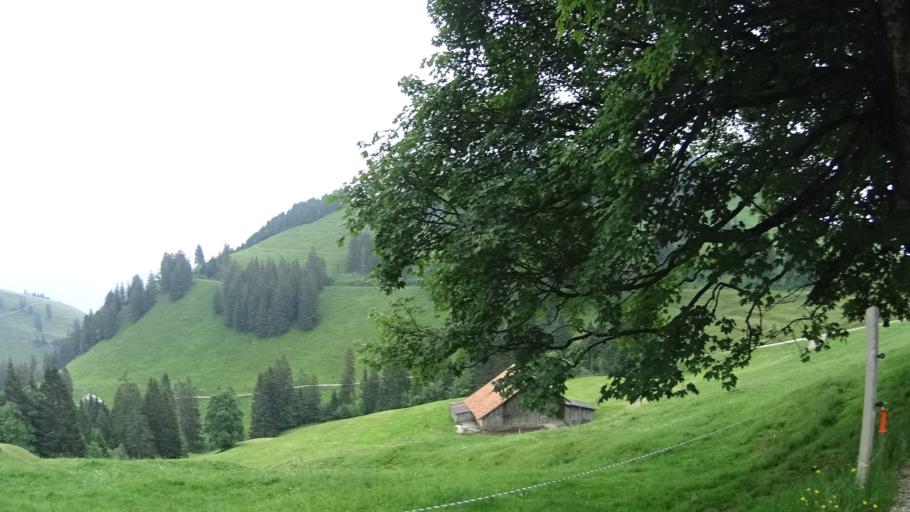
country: CH
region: Lucerne
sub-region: Lucerne-Land District
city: Vitznau
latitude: 47.0419
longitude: 8.4800
